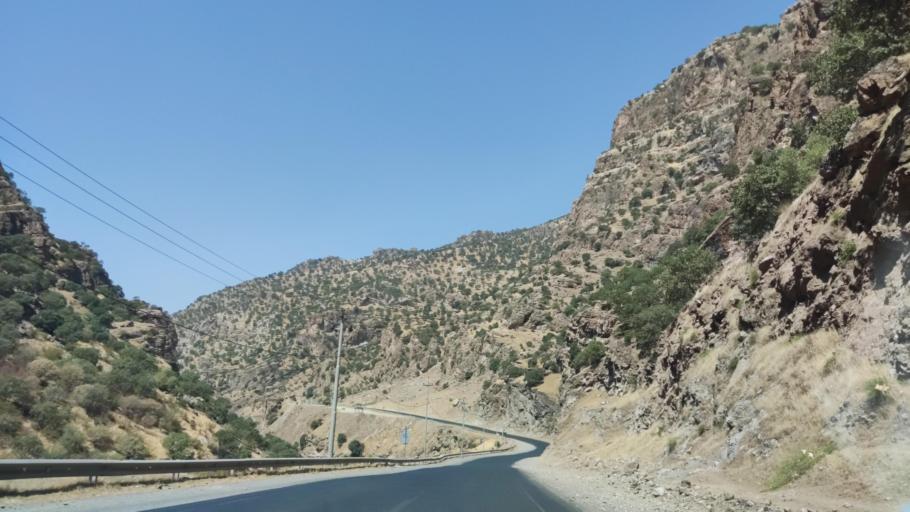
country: IQ
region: Arbil
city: Ruwandiz
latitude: 36.6306
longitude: 44.4824
